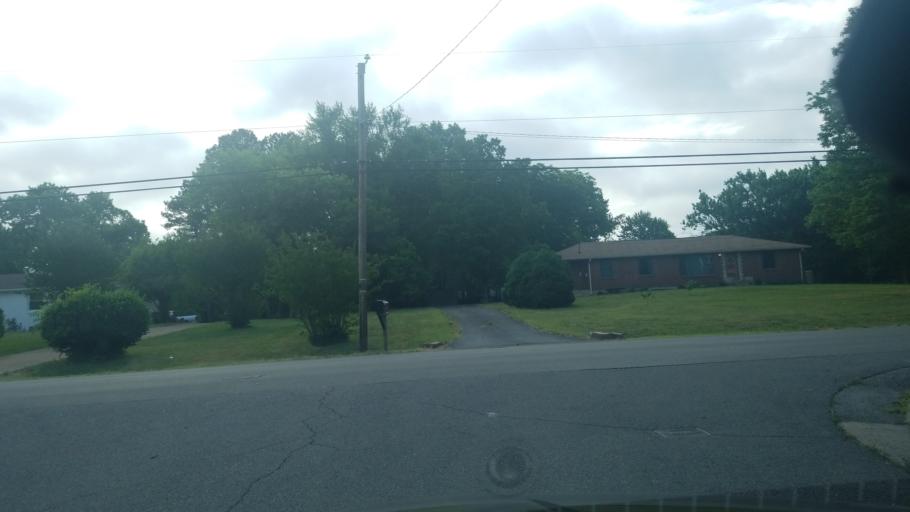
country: US
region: Tennessee
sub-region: Davidson County
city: Nashville
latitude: 36.2313
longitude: -86.7439
